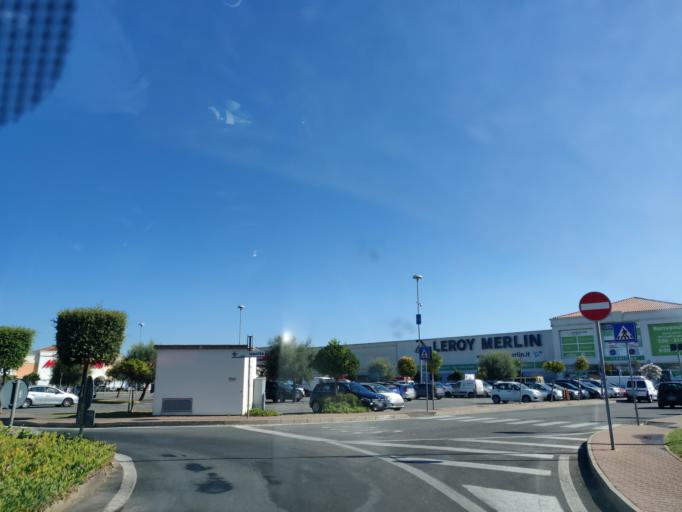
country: IT
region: Latium
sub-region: Citta metropolitana di Roma Capitale
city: Npp 23 (Parco Leonardo)
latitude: 41.8096
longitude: 12.3022
